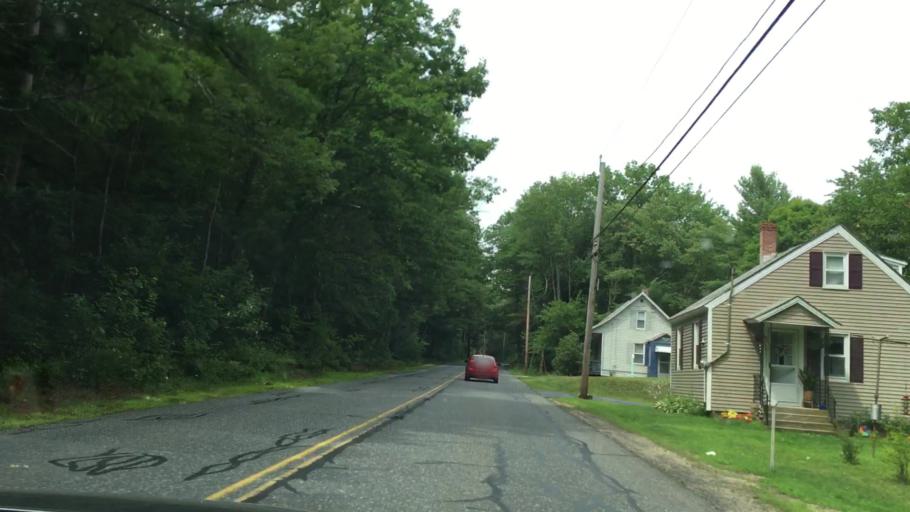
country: US
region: Massachusetts
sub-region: Worcester County
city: Winchendon
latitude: 42.6980
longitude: -72.0148
